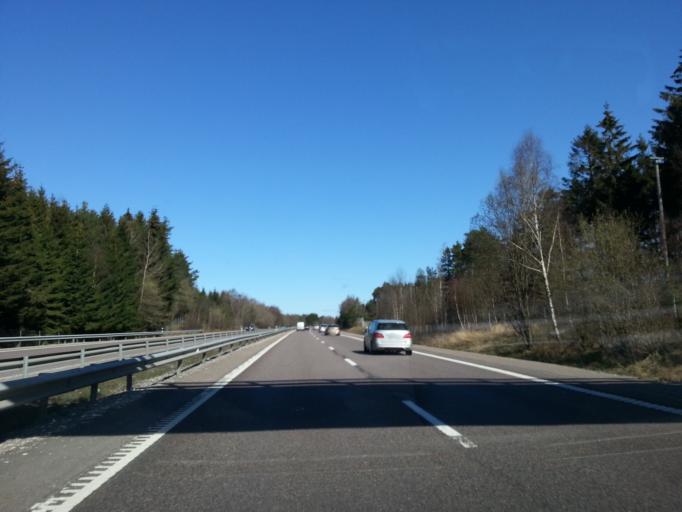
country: SE
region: Vaestra Goetaland
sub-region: Kungalvs Kommun
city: Kode
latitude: 57.9617
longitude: 11.8451
